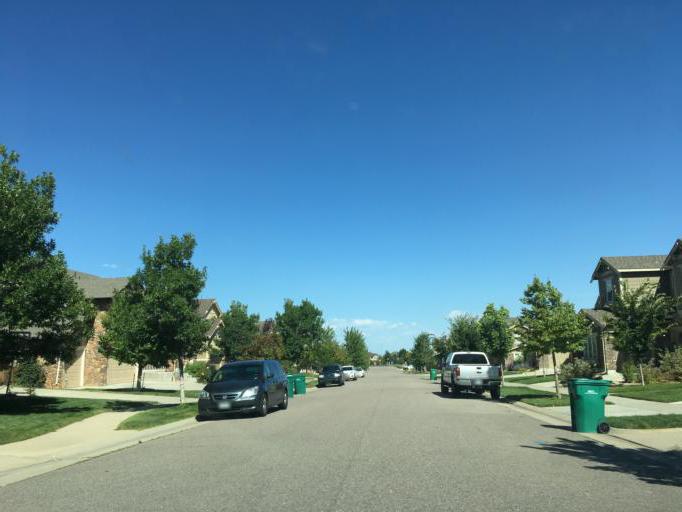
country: US
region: Colorado
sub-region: Douglas County
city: Parker
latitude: 39.6023
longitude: -104.6917
